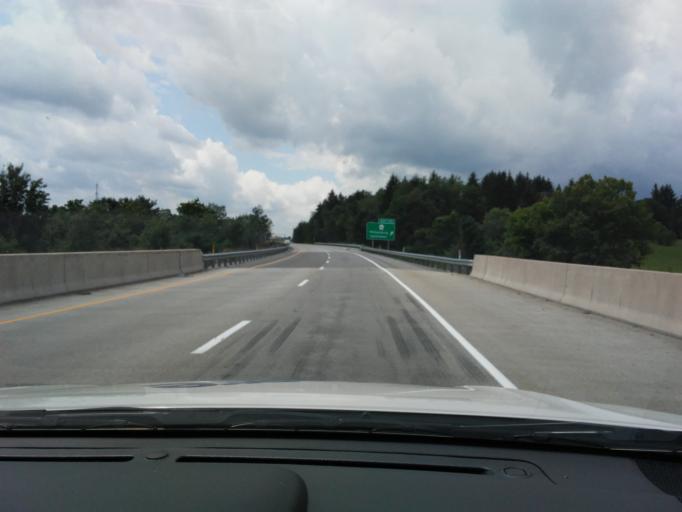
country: US
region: Pennsylvania
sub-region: Clearfield County
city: Troy
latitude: 40.9898
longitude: -78.1607
